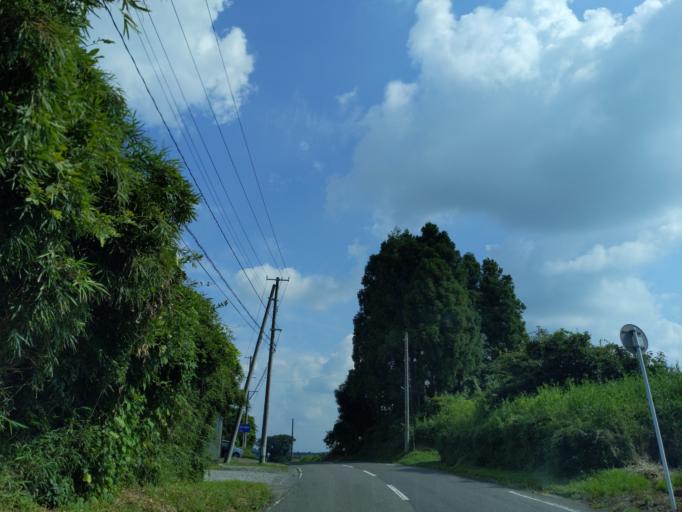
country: JP
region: Fukushima
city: Sukagawa
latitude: 37.3205
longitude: 140.3292
